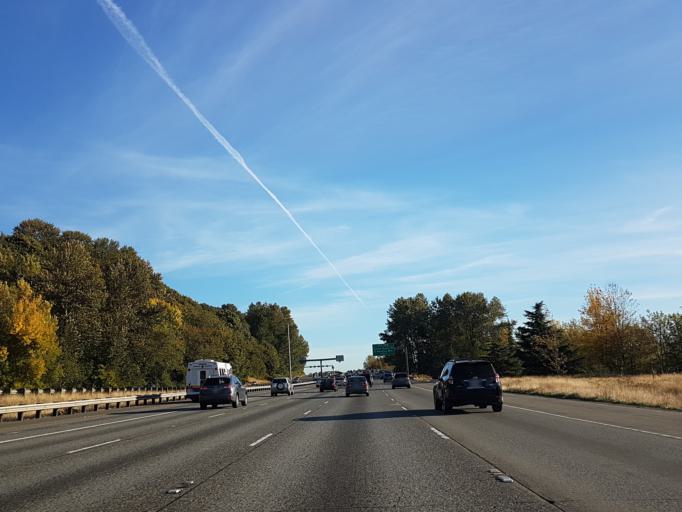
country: US
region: Washington
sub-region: King County
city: Riverton
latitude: 47.5253
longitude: -122.2922
